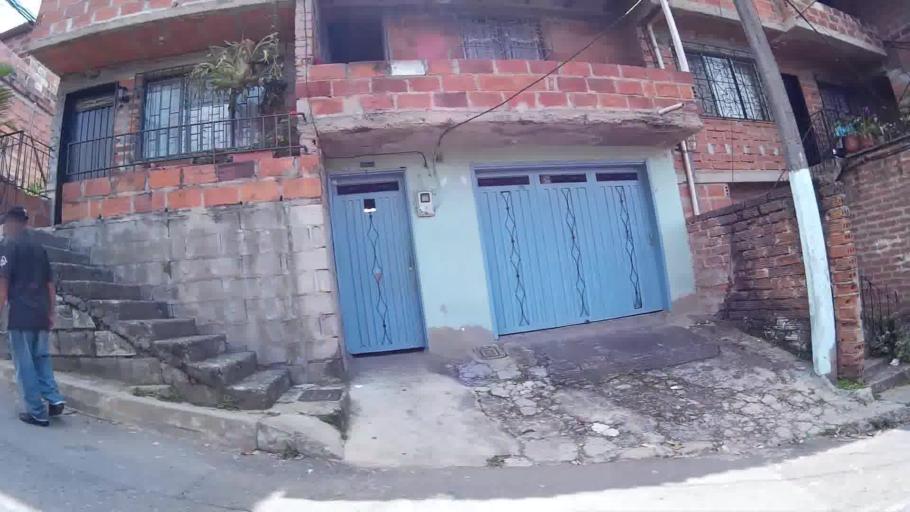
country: CO
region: Antioquia
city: Medellin
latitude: 6.2706
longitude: -75.6287
